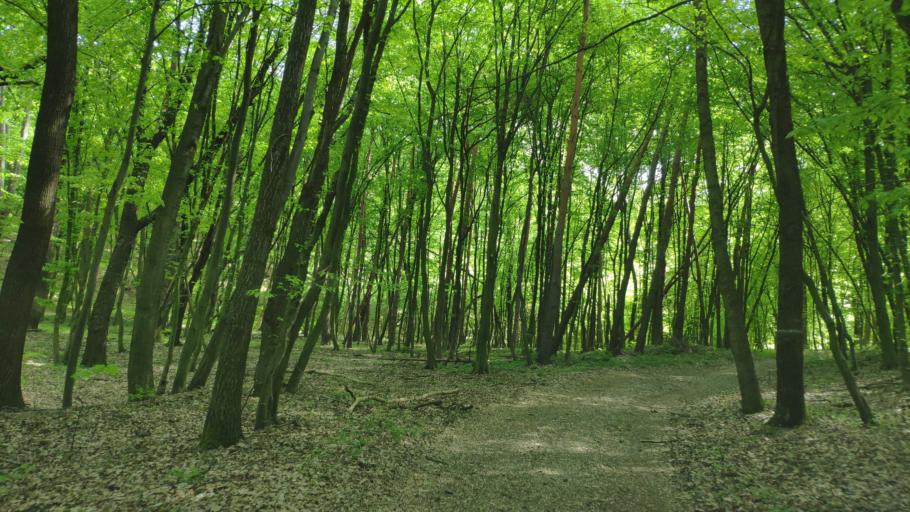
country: SK
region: Kosicky
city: Kosice
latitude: 48.6726
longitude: 21.4343
